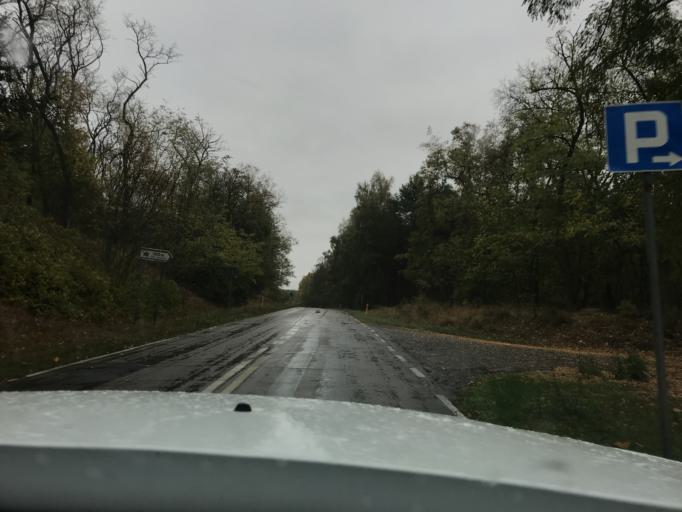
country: DE
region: Brandenburg
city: Neulewin
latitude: 52.7706
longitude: 14.3118
